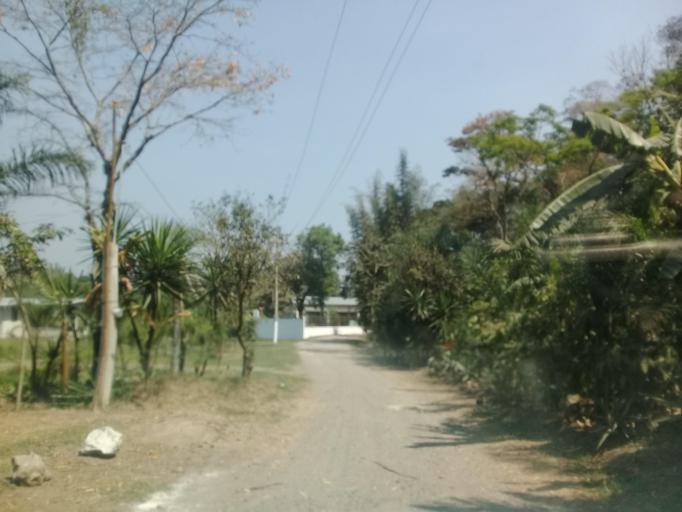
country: MX
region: Veracruz
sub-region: Ixtaczoquitlan
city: Capoluca
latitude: 18.8028
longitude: -96.9891
